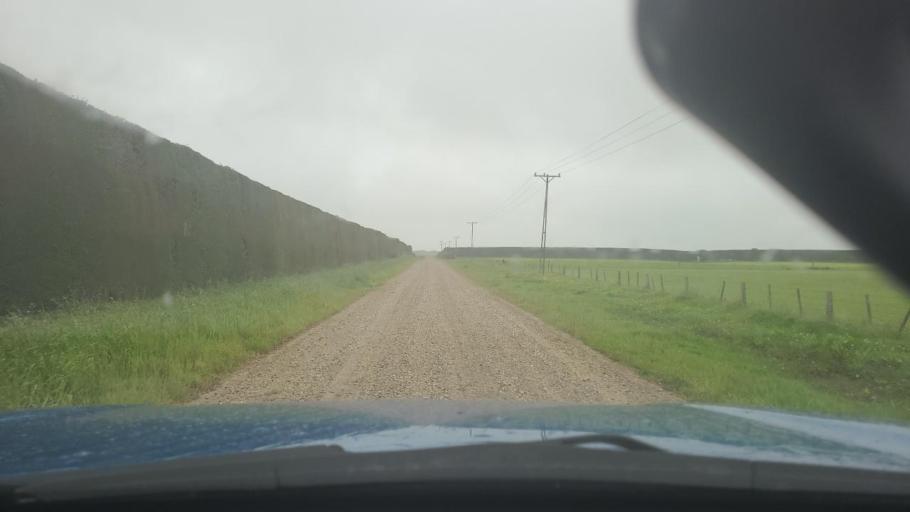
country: NZ
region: Southland
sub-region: Invercargill City
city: Invercargill
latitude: -46.4083
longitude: 168.6804
